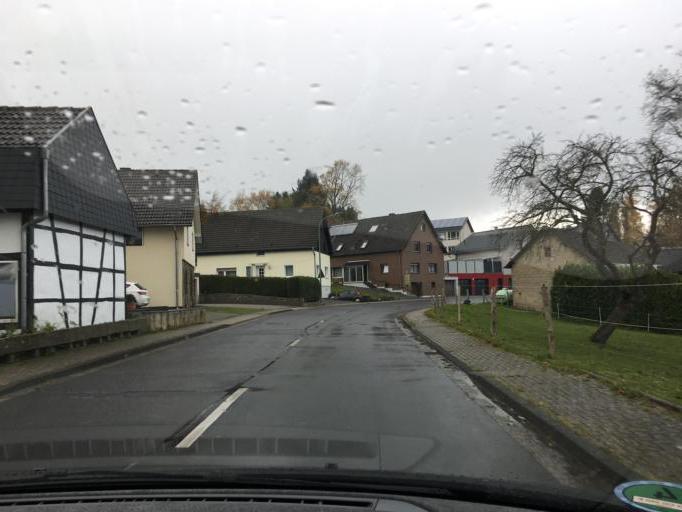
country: DE
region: North Rhine-Westphalia
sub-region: Regierungsbezirk Koln
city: Simmerath
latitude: 50.6240
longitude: 6.3556
